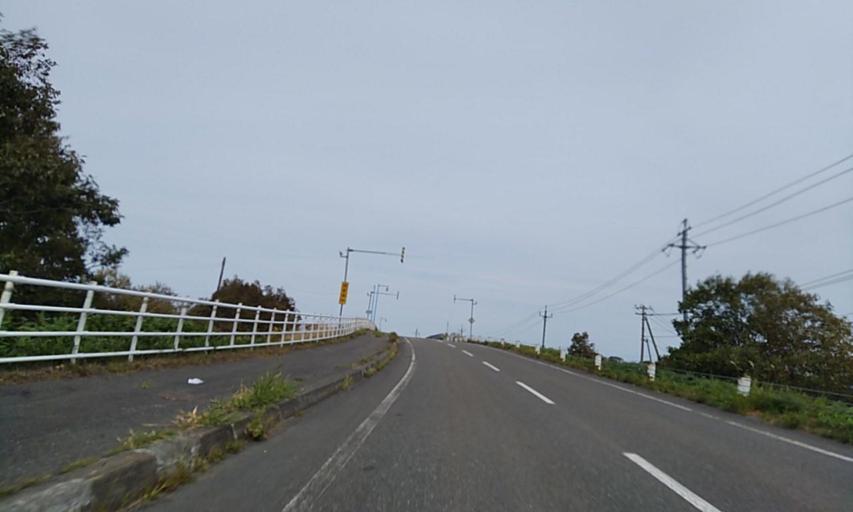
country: JP
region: Hokkaido
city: Makubetsu
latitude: 45.0035
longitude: 141.7074
